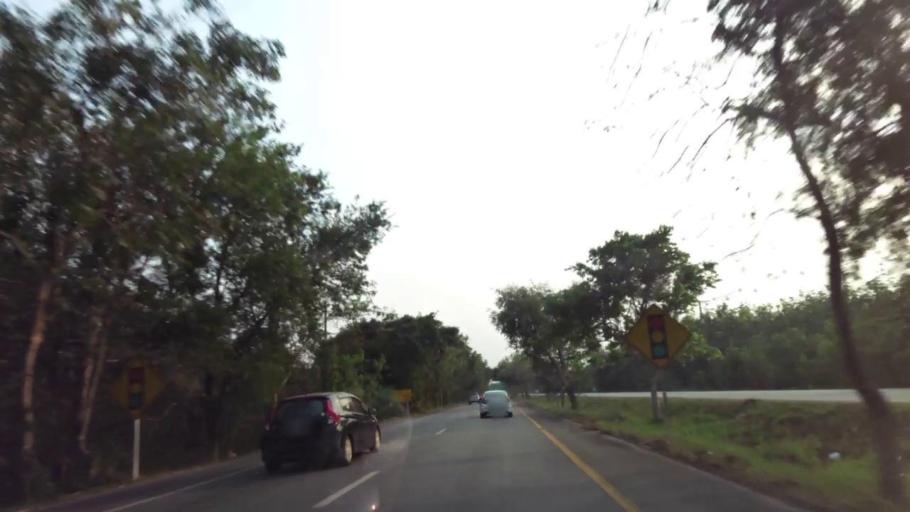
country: TH
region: Chanthaburi
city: Chanthaburi
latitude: 12.5354
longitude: 102.1576
